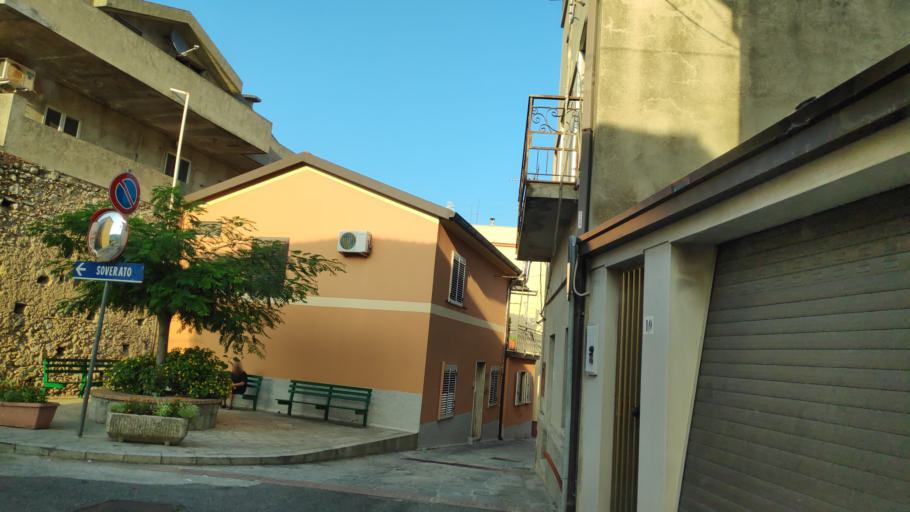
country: IT
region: Calabria
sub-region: Provincia di Catanzaro
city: Satriano
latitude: 38.6684
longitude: 16.4813
